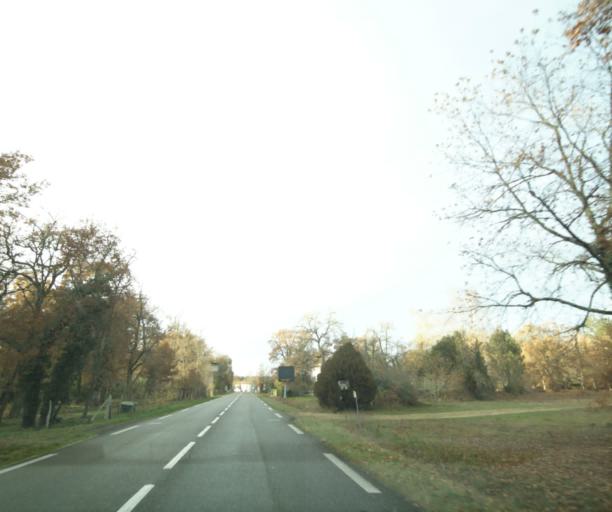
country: FR
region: Aquitaine
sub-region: Departement des Landes
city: Gabarret
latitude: 44.0639
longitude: -0.0522
